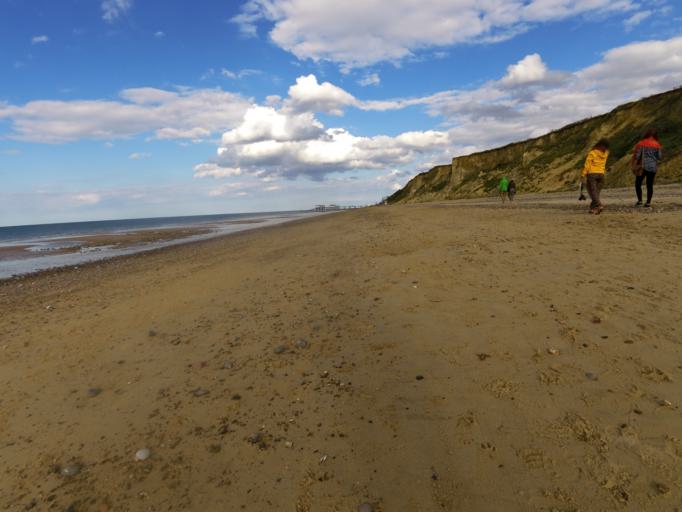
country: GB
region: England
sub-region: Norfolk
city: Cromer
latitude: 52.9357
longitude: 1.2840
